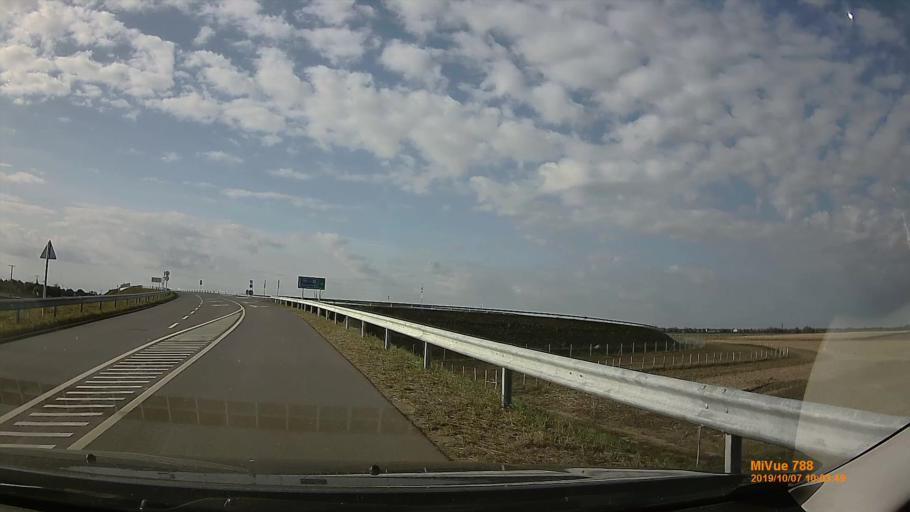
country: HU
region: Bekes
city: Kondoros
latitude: 46.7414
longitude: 20.7848
